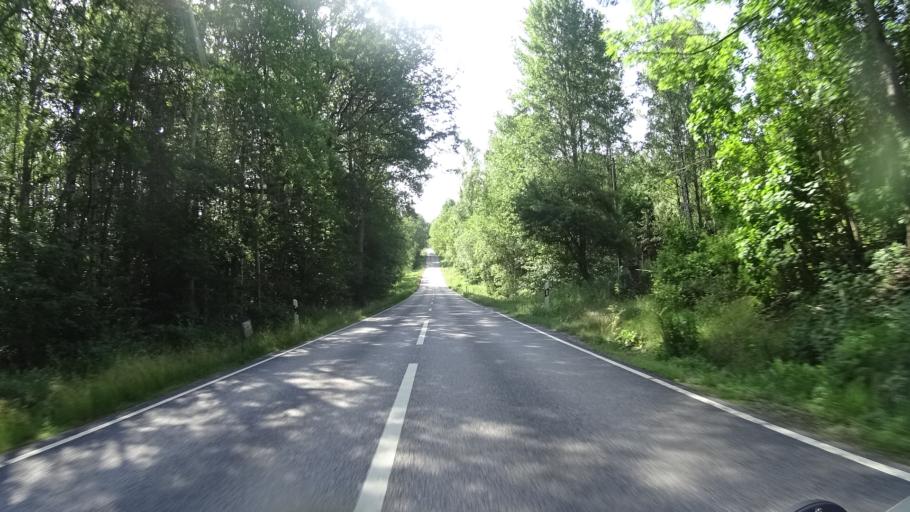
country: SE
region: Kalmar
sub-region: Vasterviks Kommun
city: Overum
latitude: 58.0778
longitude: 16.1848
